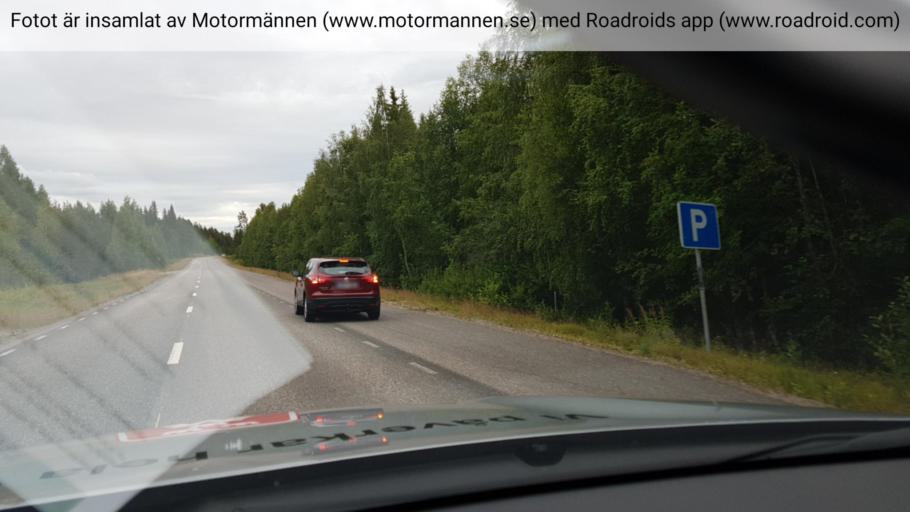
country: SE
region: Norrbotten
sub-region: Overkalix Kommun
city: OEverkalix
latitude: 66.5236
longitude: 22.7613
